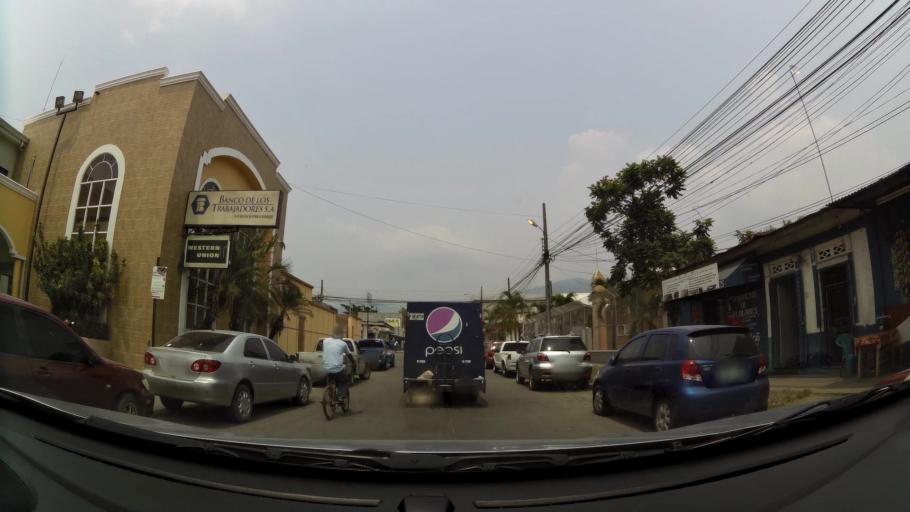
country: HN
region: Yoro
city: El Progreso
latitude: 15.4015
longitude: -87.8058
